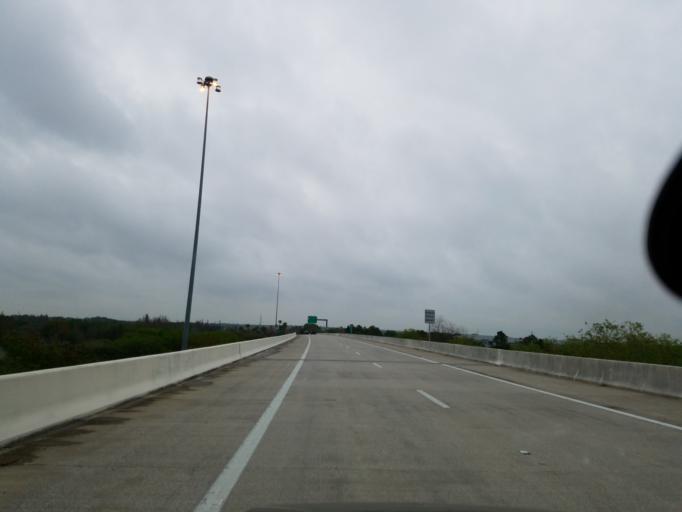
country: US
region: Florida
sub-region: Hillsborough County
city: Brandon
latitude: 27.9270
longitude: -82.3261
